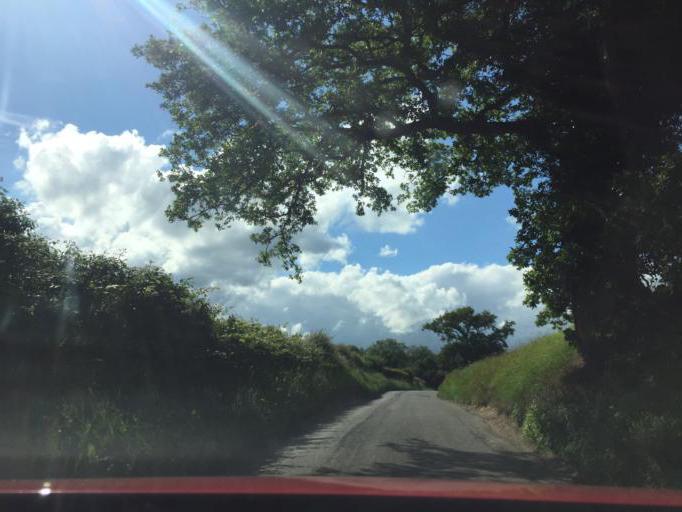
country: GB
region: England
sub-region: Hertfordshire
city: Codicote
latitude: 51.8566
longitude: -0.2541
